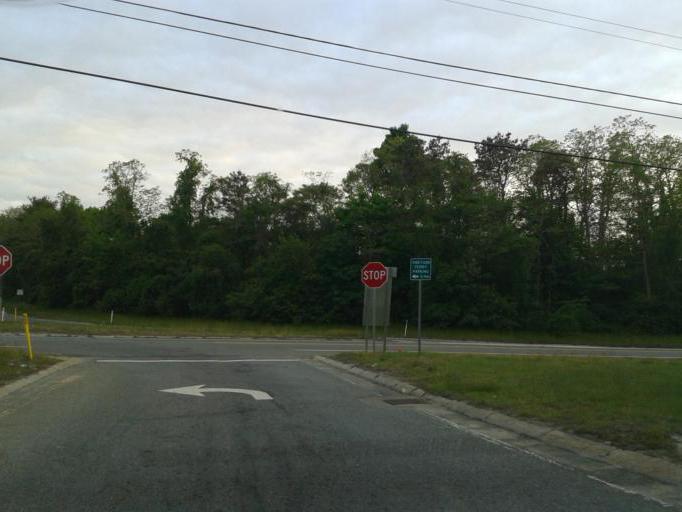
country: US
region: Massachusetts
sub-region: Barnstable County
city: West Falmouth
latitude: 41.6174
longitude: -70.6212
